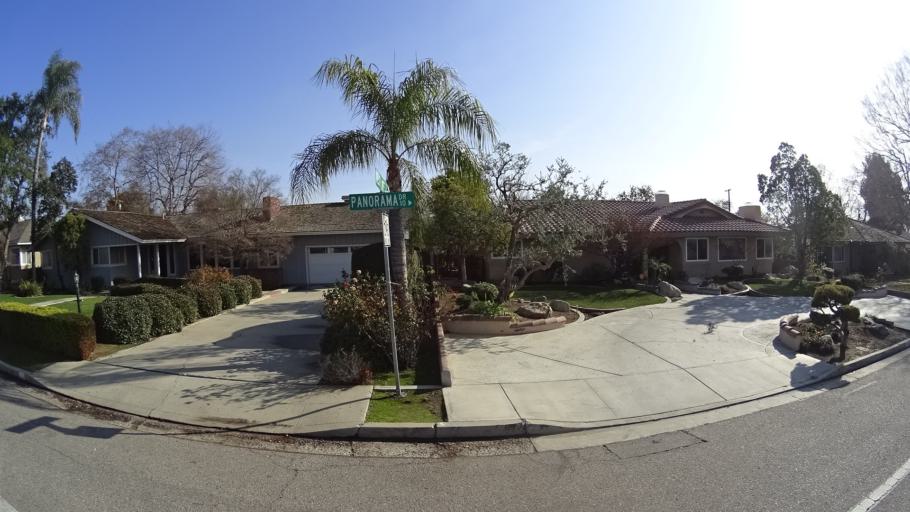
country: US
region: California
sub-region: Kern County
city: Oildale
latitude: 35.4033
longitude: -119.0009
